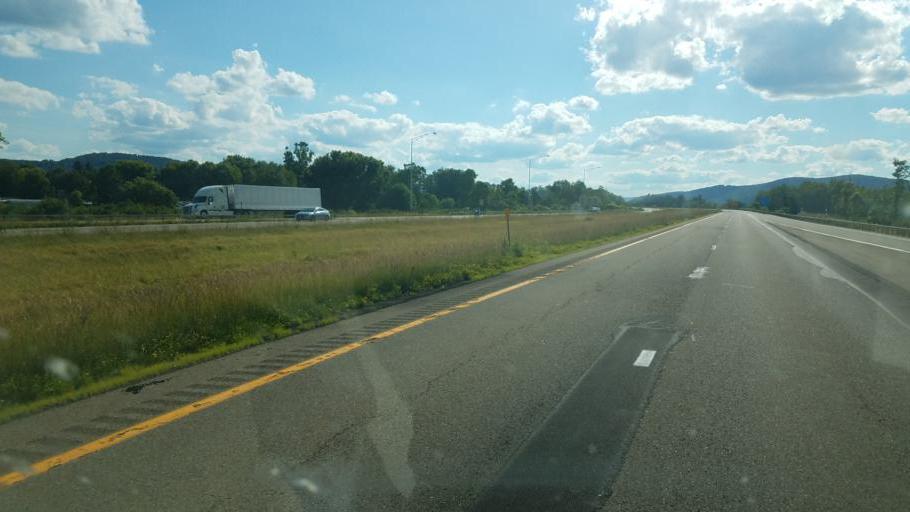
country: US
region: New York
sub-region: Cattaraugus County
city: Allegany
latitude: 42.1029
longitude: -78.5109
